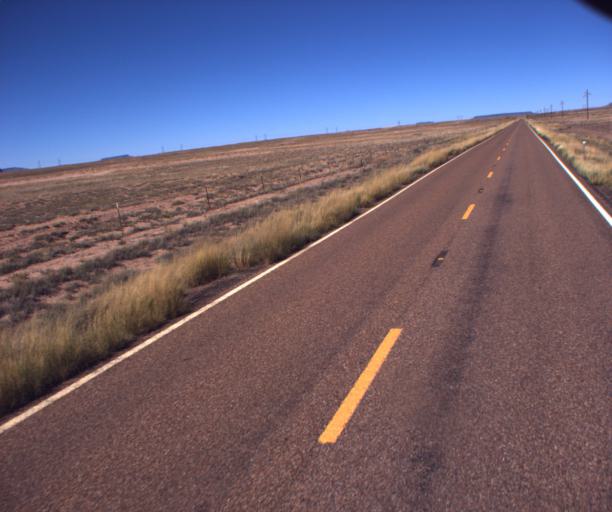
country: US
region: Arizona
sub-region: Navajo County
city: Holbrook
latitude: 35.1205
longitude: -110.0927
